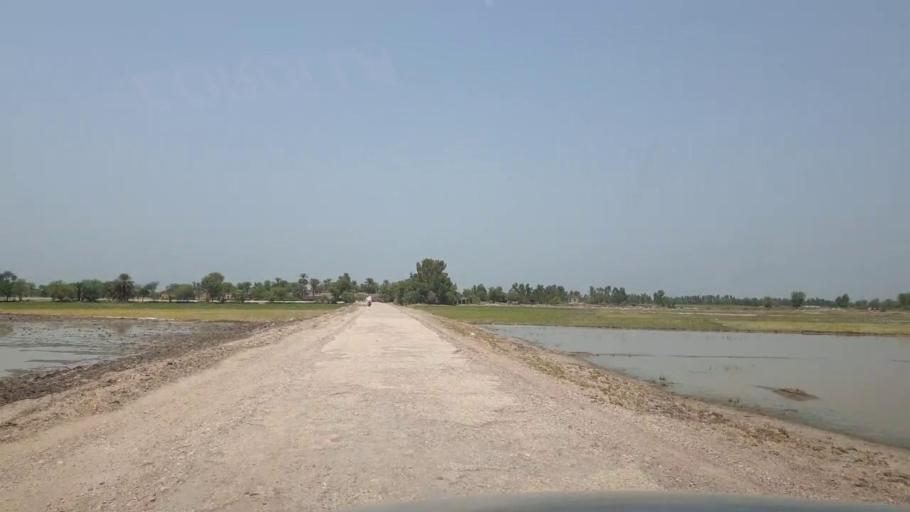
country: PK
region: Sindh
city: Garhi Yasin
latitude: 27.8677
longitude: 68.4565
